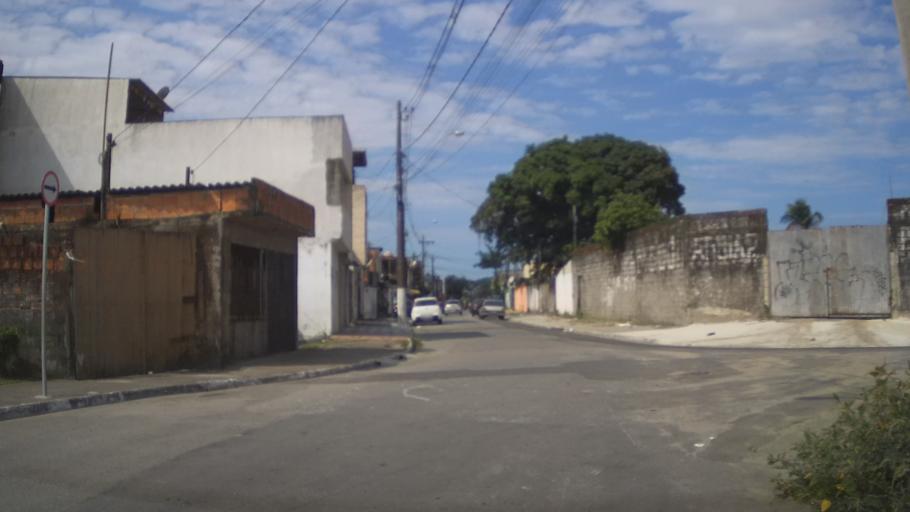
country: BR
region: Sao Paulo
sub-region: Praia Grande
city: Praia Grande
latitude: -24.0036
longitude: -46.4353
